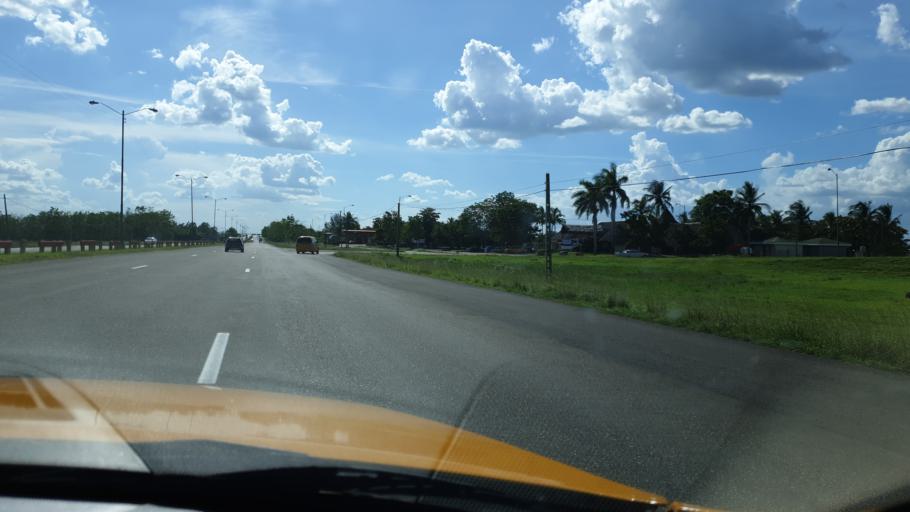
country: CU
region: Cienfuegos
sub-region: Municipio de Aguada de Pasajeros
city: Aguada de Pasajeros
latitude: 22.4040
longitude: -80.8640
